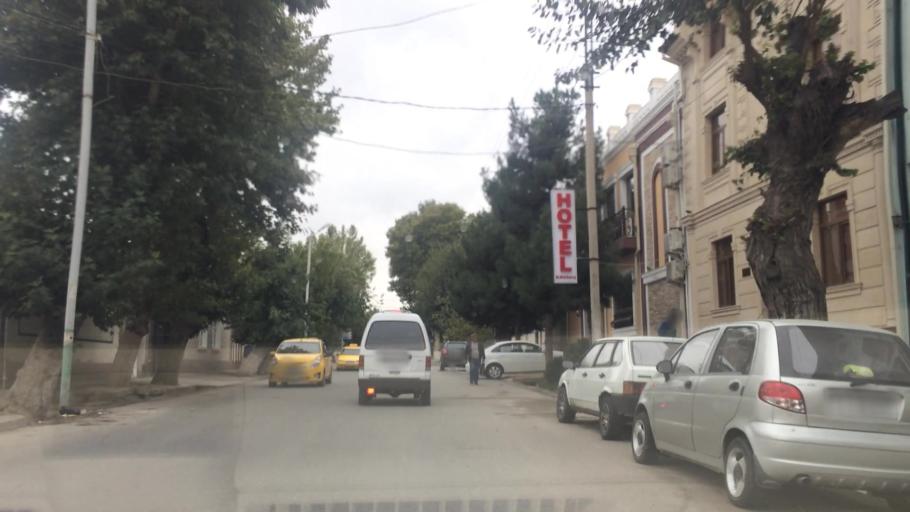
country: UZ
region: Samarqand
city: Samarqand
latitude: 39.6620
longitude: 66.9763
